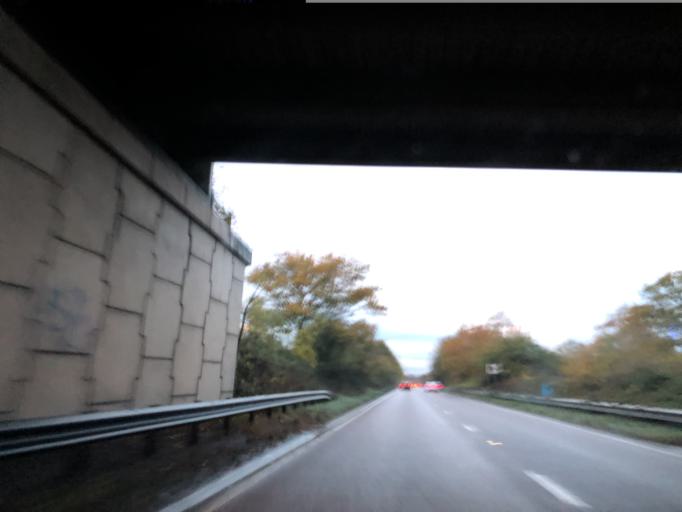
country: GB
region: England
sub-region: Solihull
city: Meriden
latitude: 52.4429
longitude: -1.6513
